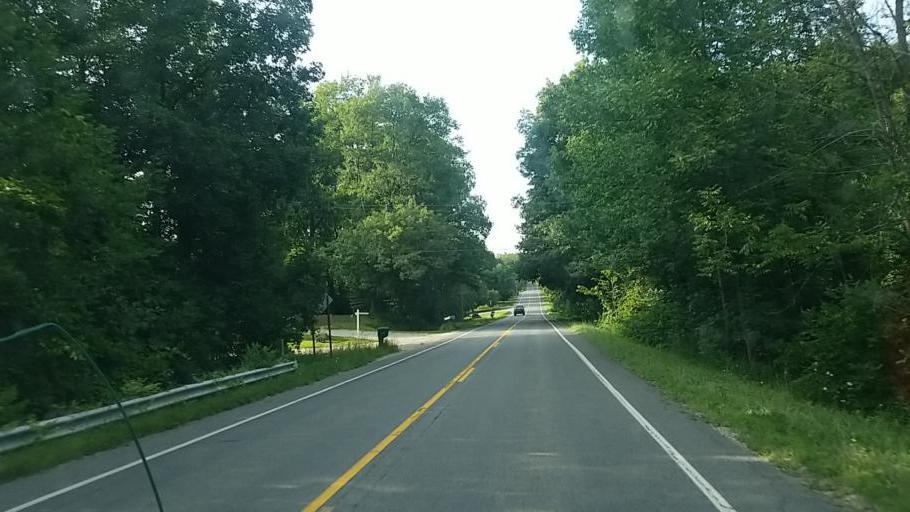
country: US
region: Michigan
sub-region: Montcalm County
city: Greenville
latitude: 43.1226
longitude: -85.3522
